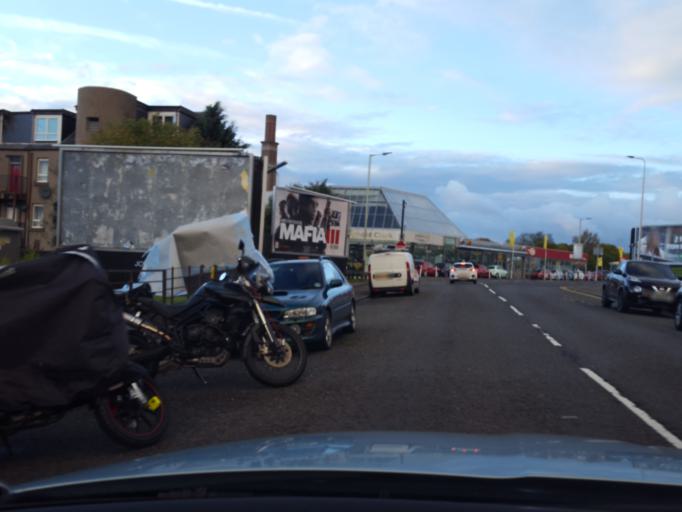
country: GB
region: Scotland
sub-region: Dundee City
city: Dundee
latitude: 56.4703
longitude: -2.9995
